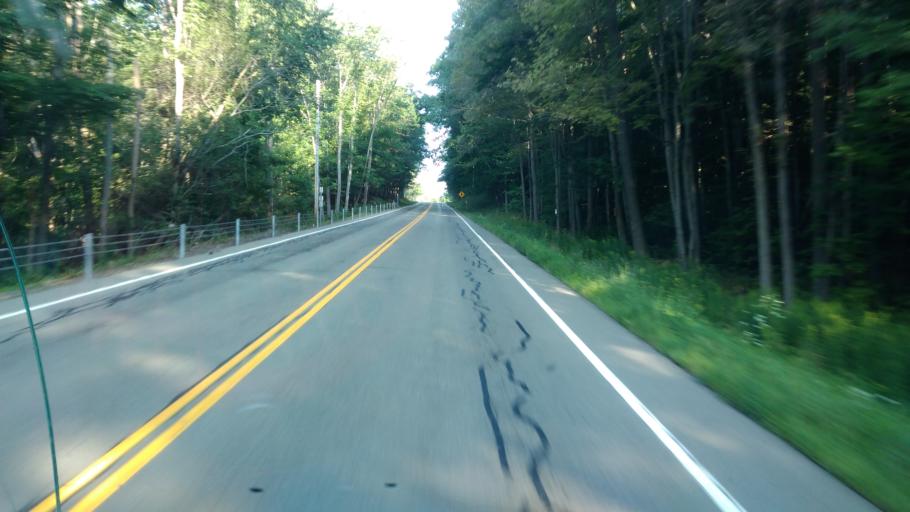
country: US
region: New York
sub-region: Allegany County
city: Andover
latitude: 42.1454
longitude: -77.6830
